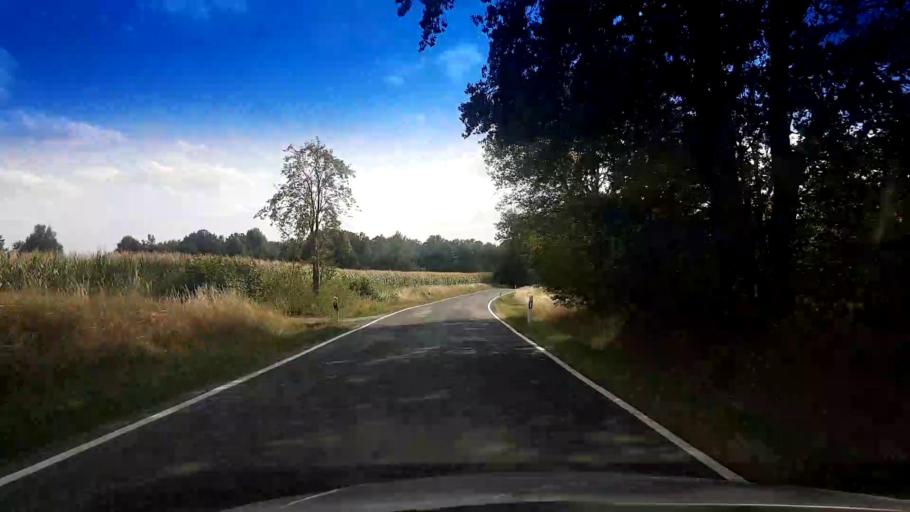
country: DE
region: Bavaria
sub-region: Upper Palatinate
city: Tirschenreuth
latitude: 49.9132
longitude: 12.3921
